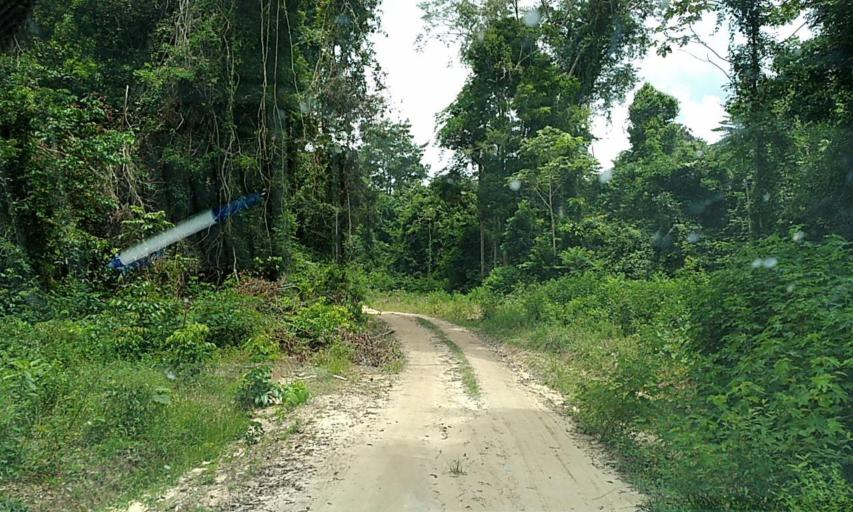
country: BR
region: Para
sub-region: Altamira
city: Altamira
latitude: -3.0582
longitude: -52.9072
